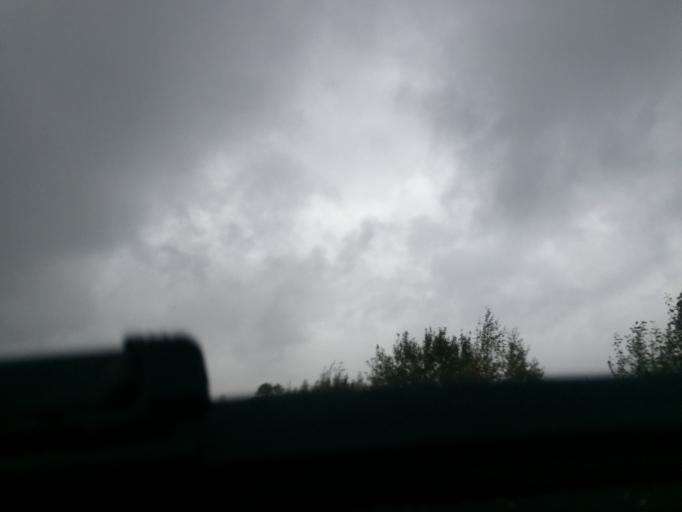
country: LV
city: Tireli
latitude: 56.7276
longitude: 23.5037
